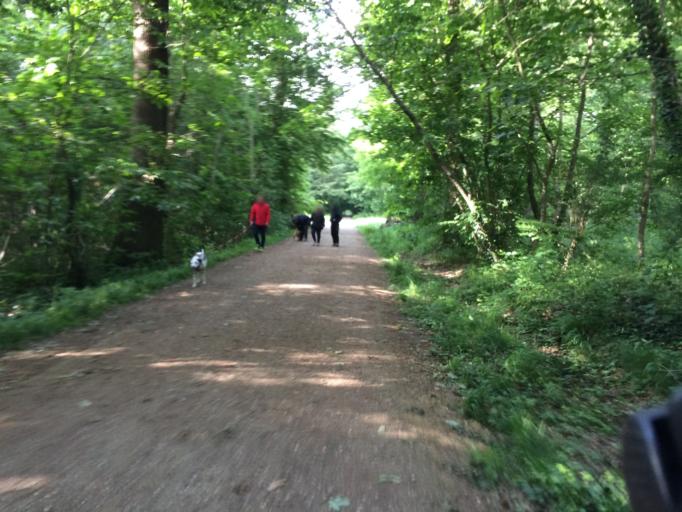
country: FR
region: Ile-de-France
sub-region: Departement de l'Essonne
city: Igny
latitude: 48.7548
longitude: 2.2422
